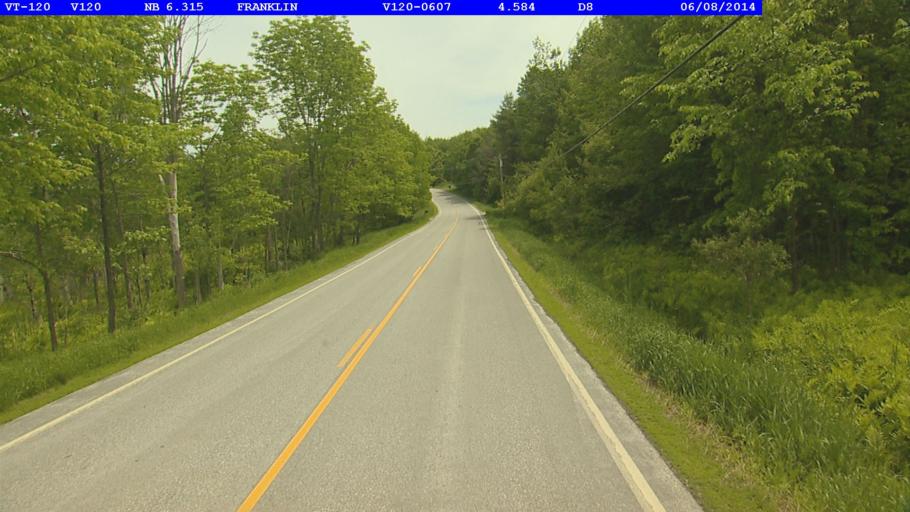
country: US
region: Vermont
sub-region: Franklin County
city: Enosburg Falls
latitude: 44.9866
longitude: -72.9017
